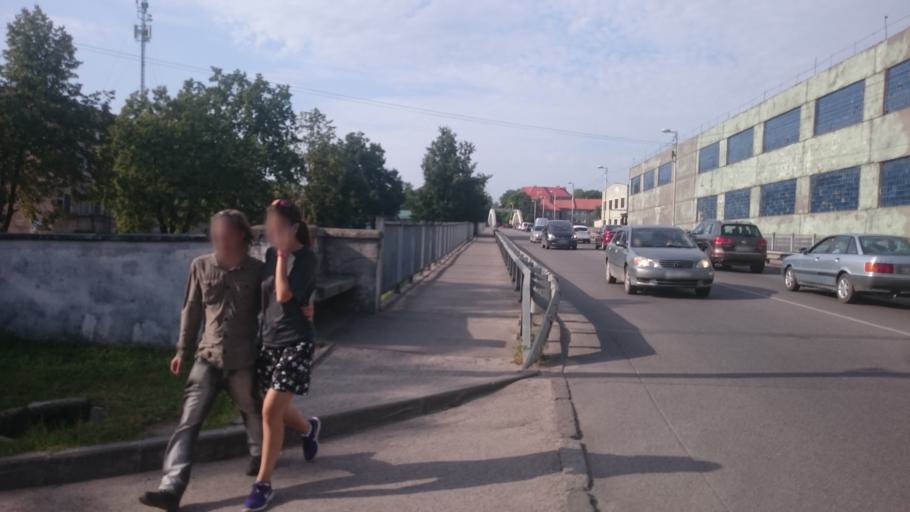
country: RU
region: Kaliningrad
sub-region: Gorod Kaliningrad
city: Kaliningrad
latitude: 54.7086
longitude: 20.4588
